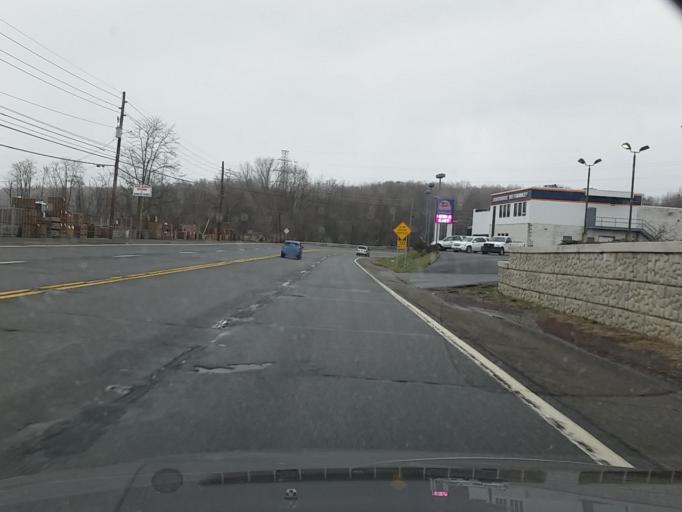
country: US
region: Pennsylvania
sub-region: Luzerne County
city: Plymouth
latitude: 41.2105
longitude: -75.9666
